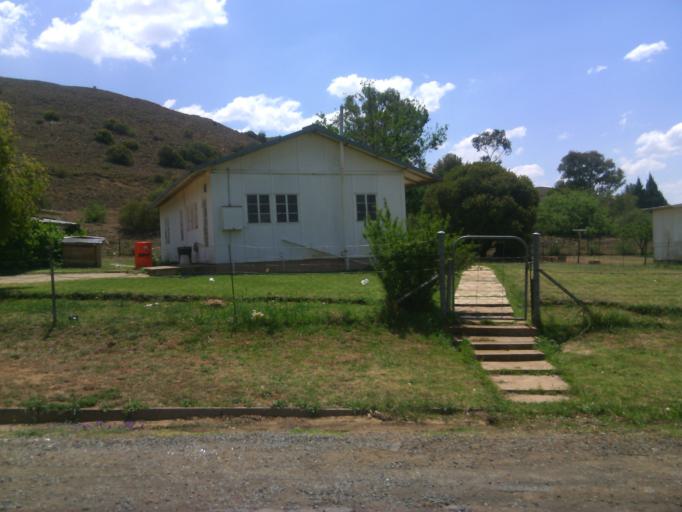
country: ZA
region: Orange Free State
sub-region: Xhariep District Municipality
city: Dewetsdorp
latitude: -29.5806
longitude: 26.6621
